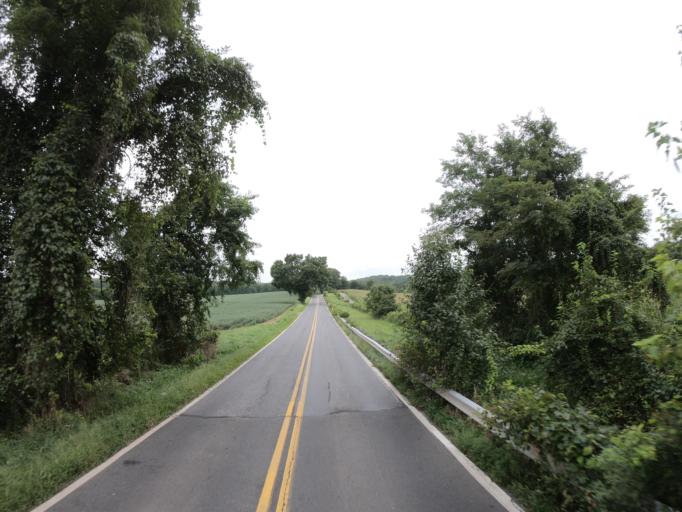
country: US
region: Maryland
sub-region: Montgomery County
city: Redland
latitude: 39.2162
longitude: -77.1125
